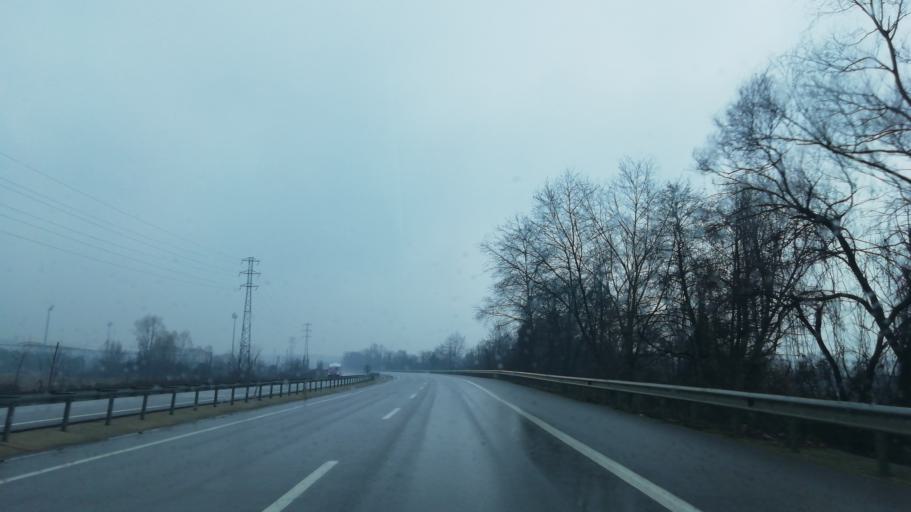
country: TR
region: Sakarya
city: Akyazi
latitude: 40.6707
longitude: 30.5882
